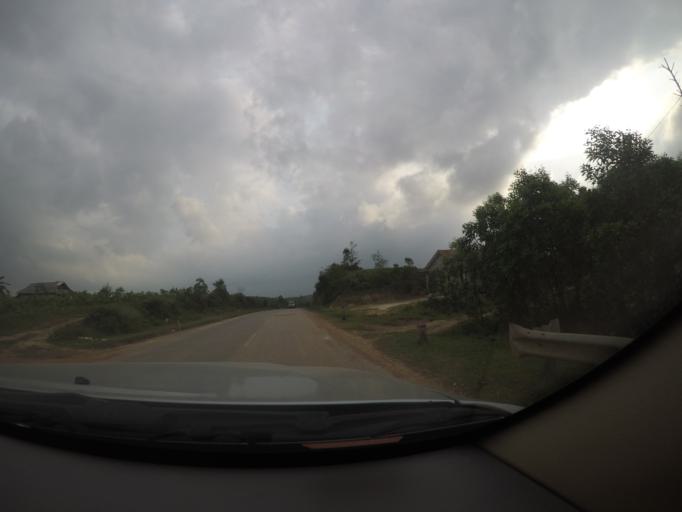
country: VN
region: Quang Tri
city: Ho Xa
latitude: 17.0738
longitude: 106.8615
